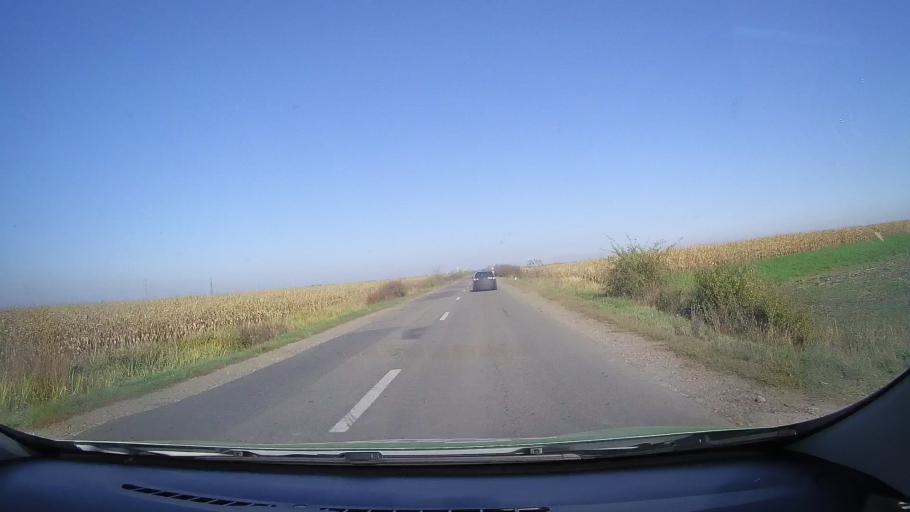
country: RO
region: Satu Mare
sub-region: Comuna Cauas
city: Cauas
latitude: 47.6118
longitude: 22.5386
